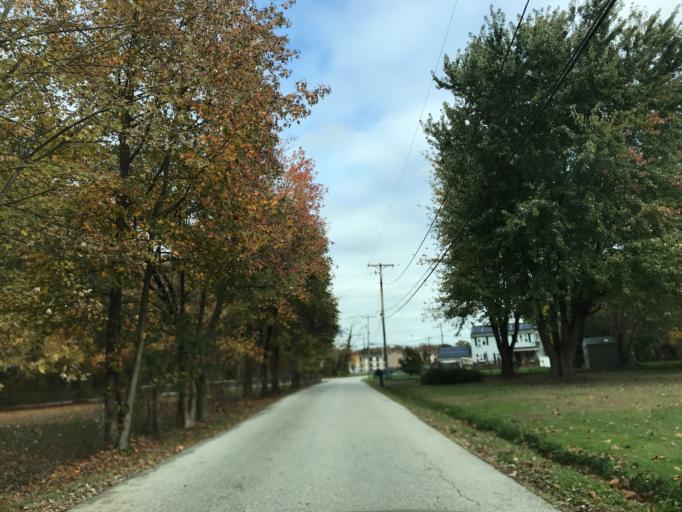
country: US
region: Maryland
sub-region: Baltimore County
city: Bowleys Quarters
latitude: 39.3285
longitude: -76.3971
